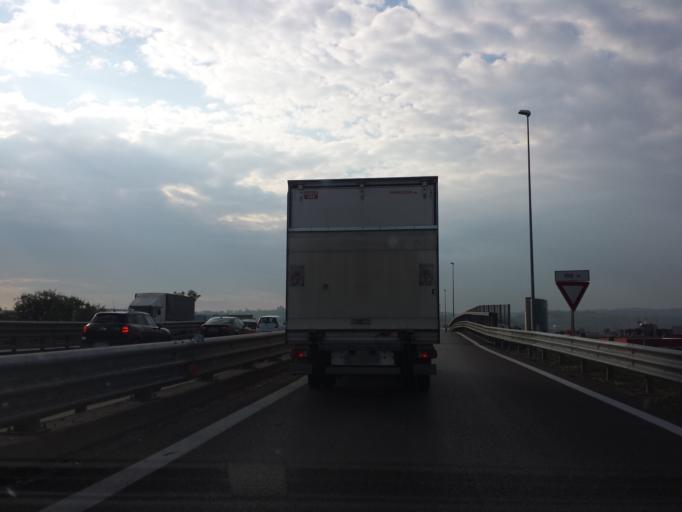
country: IT
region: Veneto
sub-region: Provincia di Vicenza
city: Creazzo
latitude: 45.5330
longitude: 11.5085
